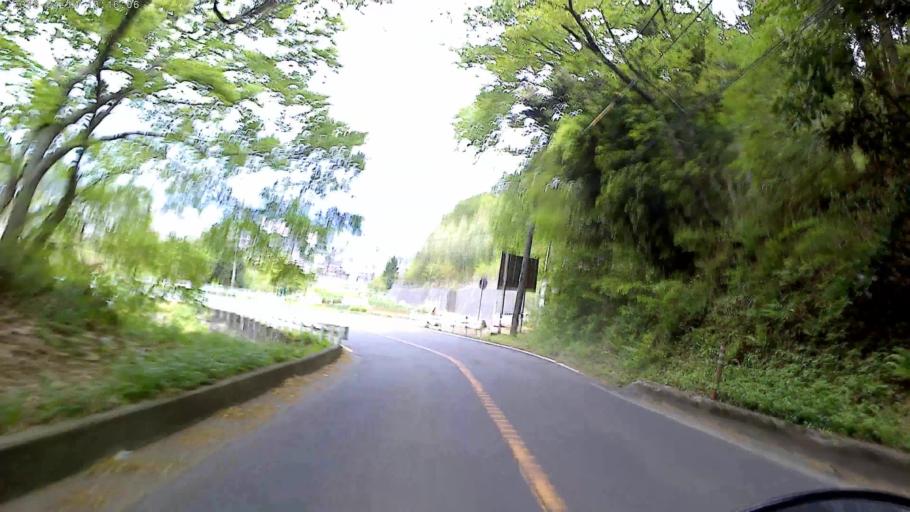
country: JP
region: Kanagawa
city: Hadano
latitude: 35.3395
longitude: 139.2364
